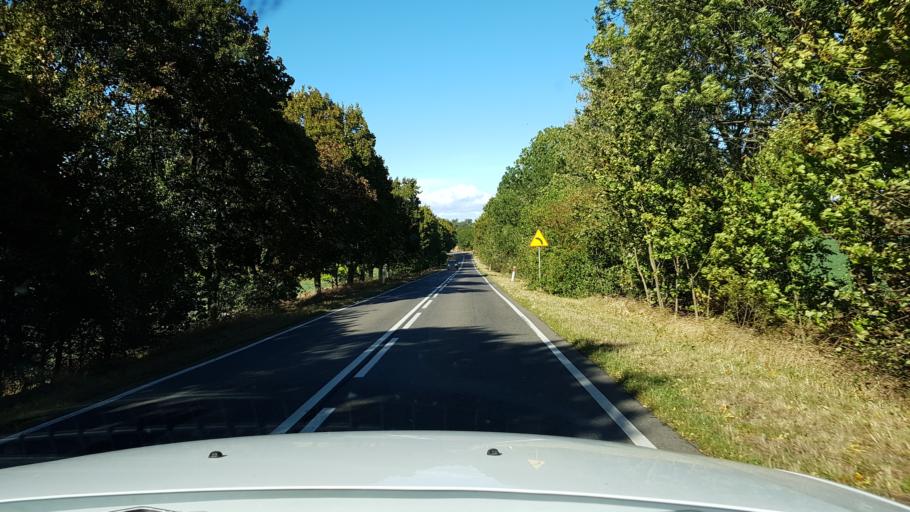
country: PL
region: West Pomeranian Voivodeship
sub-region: Powiat gryfinski
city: Banie
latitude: 53.1511
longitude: 14.6061
